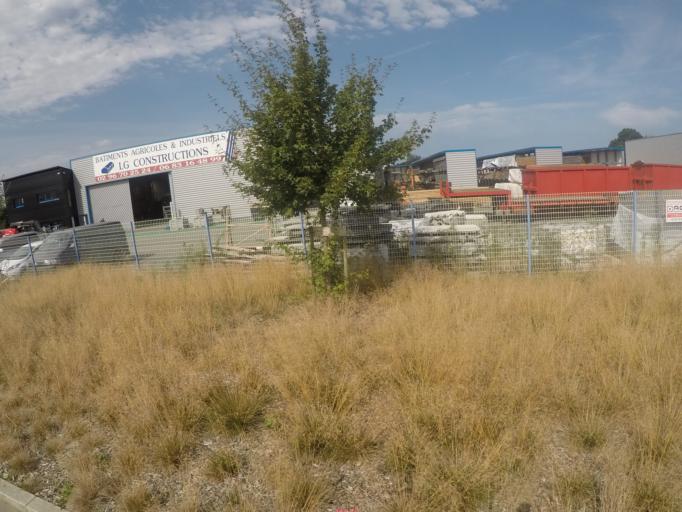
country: FR
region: Brittany
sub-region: Departement des Cotes-d'Armor
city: Lanvollon
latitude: 48.6407
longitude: -2.9893
